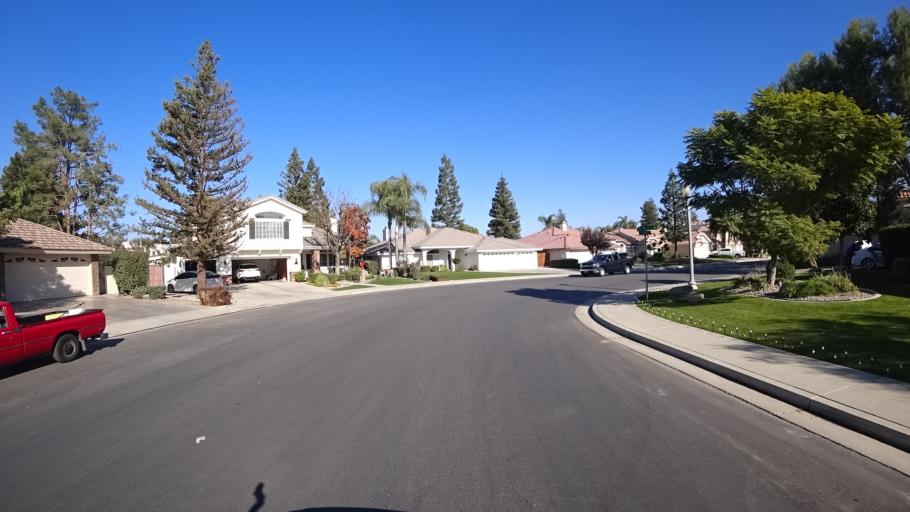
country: US
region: California
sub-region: Kern County
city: Greenacres
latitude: 35.3458
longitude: -119.1248
